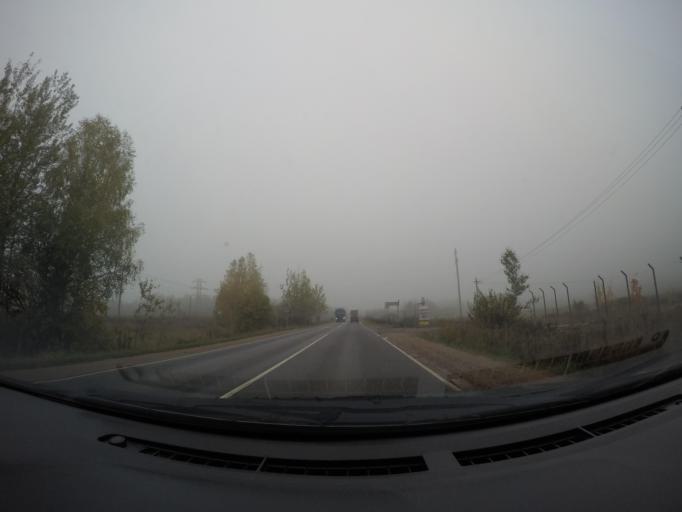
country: RU
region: Moskovskaya
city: Kostrovo
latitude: 55.8684
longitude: 36.5909
